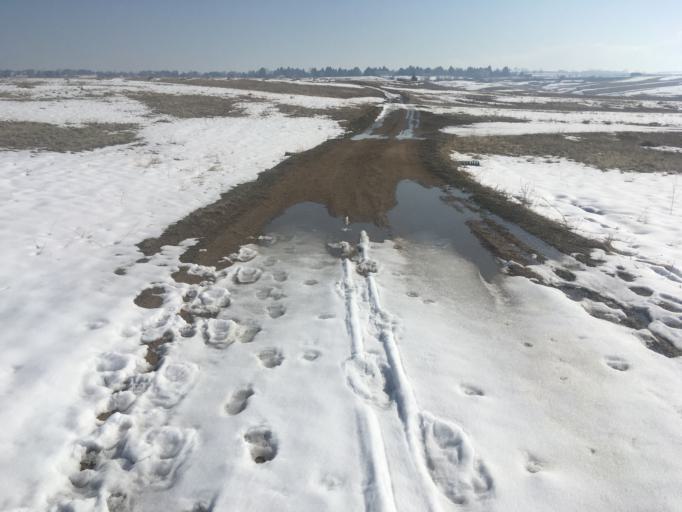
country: US
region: Colorado
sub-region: Boulder County
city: Lafayette
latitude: 39.9708
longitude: -105.0582
